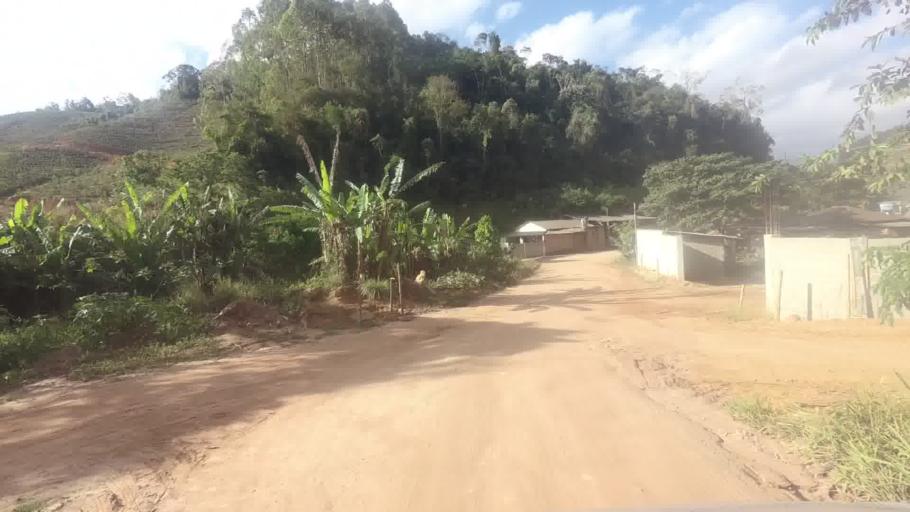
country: BR
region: Espirito Santo
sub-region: Sao Jose Do Calcado
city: Sao Jose do Calcado
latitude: -20.9744
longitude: -41.5110
